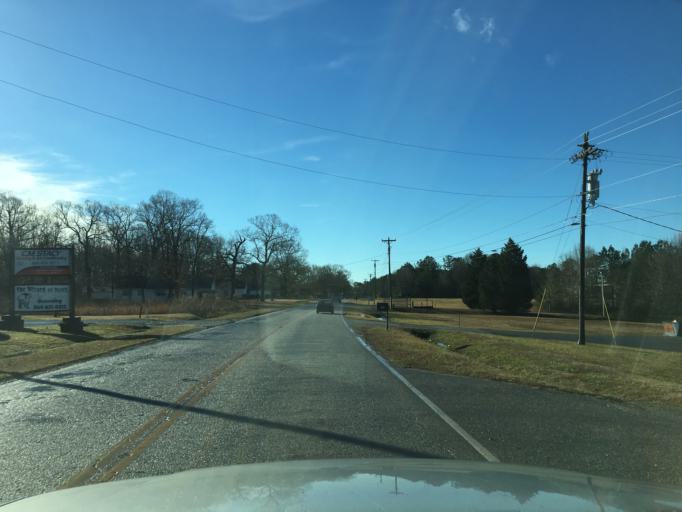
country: US
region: South Carolina
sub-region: Spartanburg County
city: Cowpens
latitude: 35.0137
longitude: -81.8725
